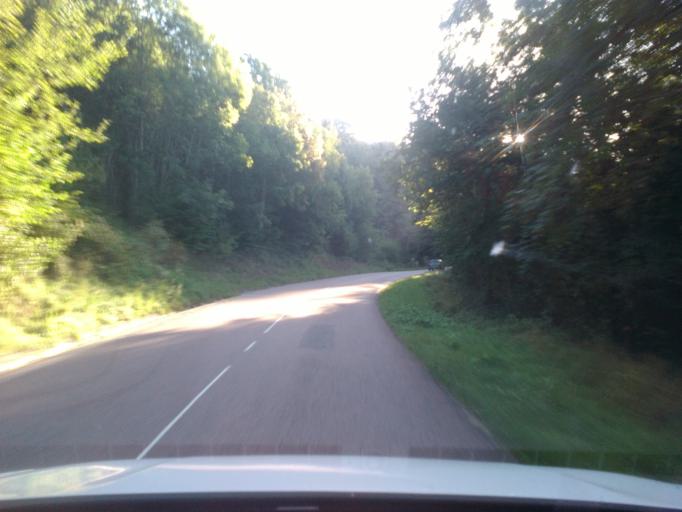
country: FR
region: Lorraine
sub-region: Departement des Vosges
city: Senones
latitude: 48.3376
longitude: 7.0030
